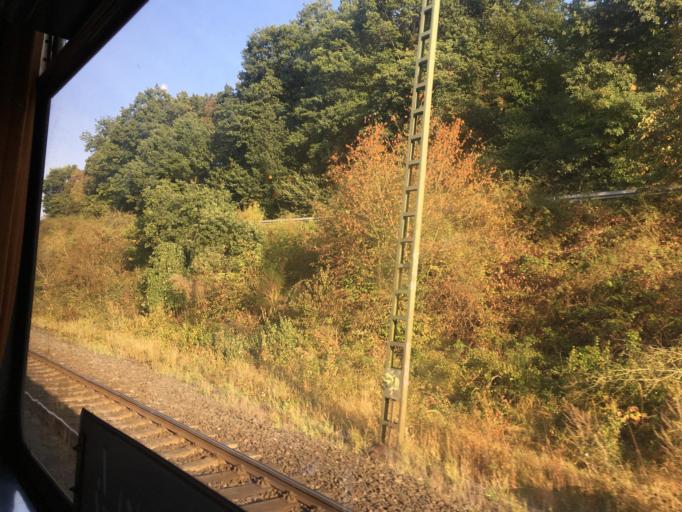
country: DE
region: North Rhine-Westphalia
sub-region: Regierungsbezirk Arnsberg
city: Frondenberg
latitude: 51.4729
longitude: 7.7519
